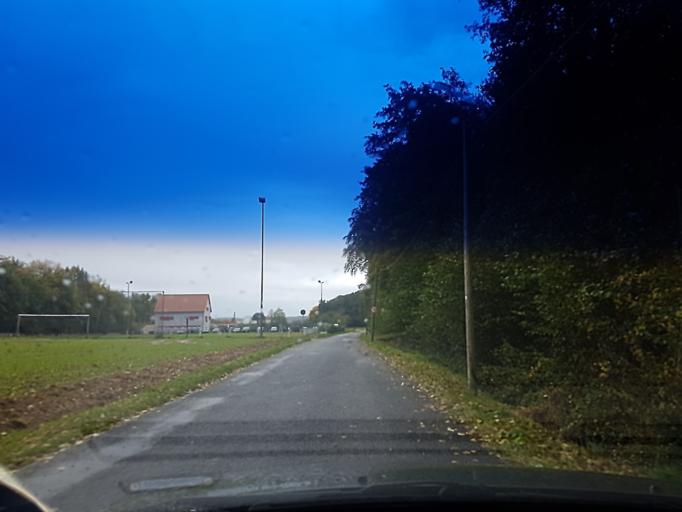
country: DE
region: Bavaria
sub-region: Regierungsbezirk Mittelfranken
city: Wachenroth
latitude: 49.7556
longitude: 10.6989
